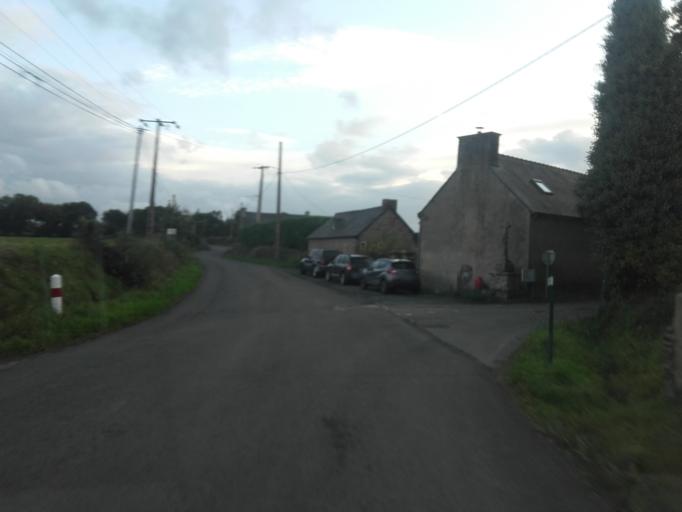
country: FR
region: Brittany
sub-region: Departement des Cotes-d'Armor
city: Plouha
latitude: 48.6688
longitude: -2.9311
